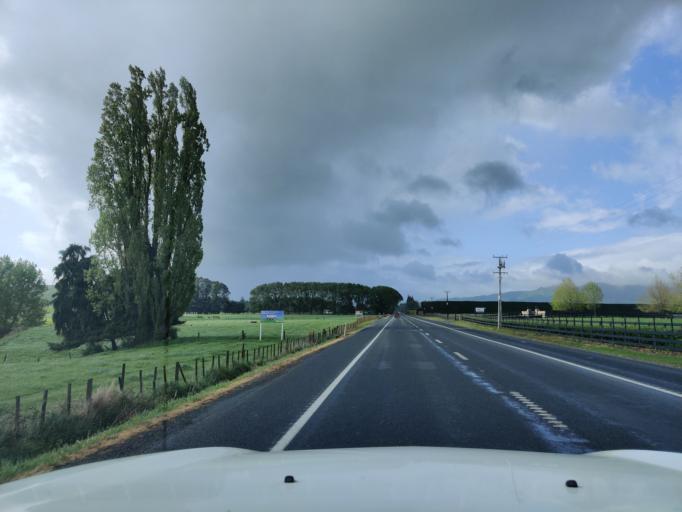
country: NZ
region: Waikato
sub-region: Waipa District
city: Cambridge
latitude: -37.9307
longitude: 175.5718
